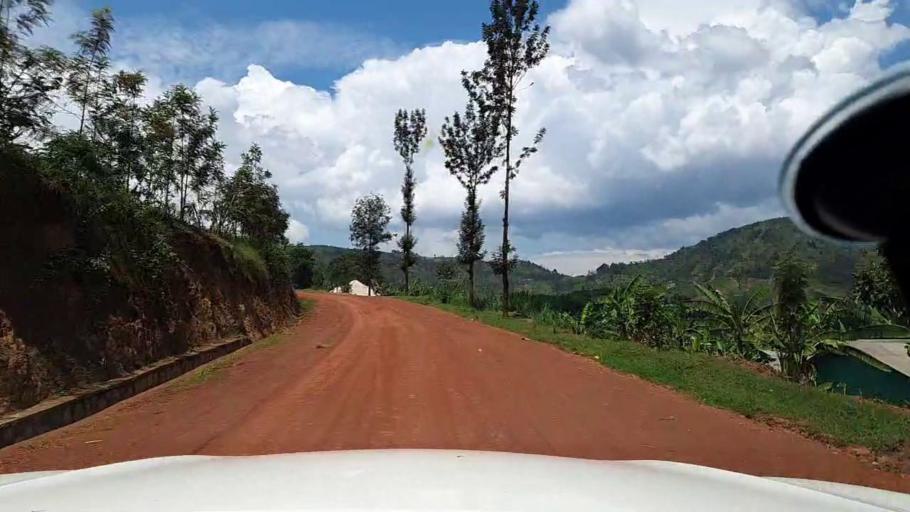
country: RW
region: Northern Province
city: Byumba
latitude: -1.6904
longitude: 29.8262
